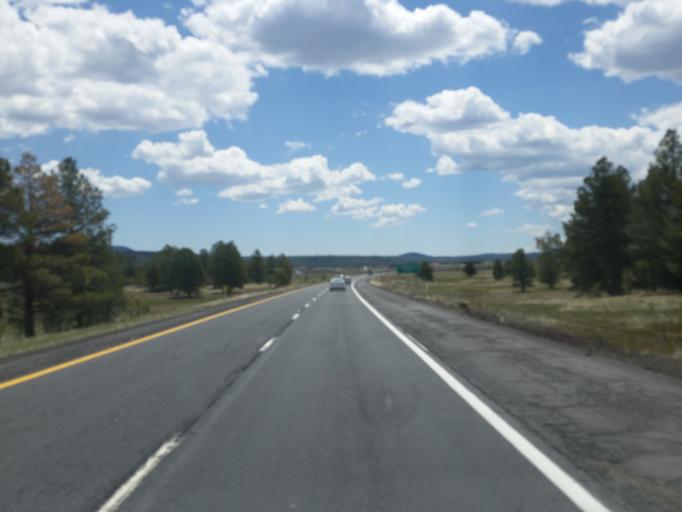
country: US
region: Arizona
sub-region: Coconino County
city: Parks
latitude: 35.2449
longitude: -111.8425
